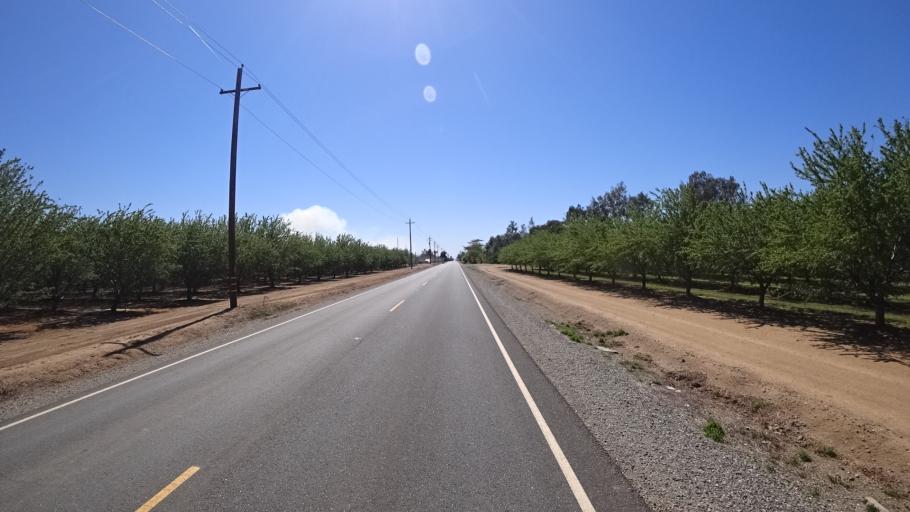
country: US
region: California
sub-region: Glenn County
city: Willows
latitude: 39.5155
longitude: -122.2492
